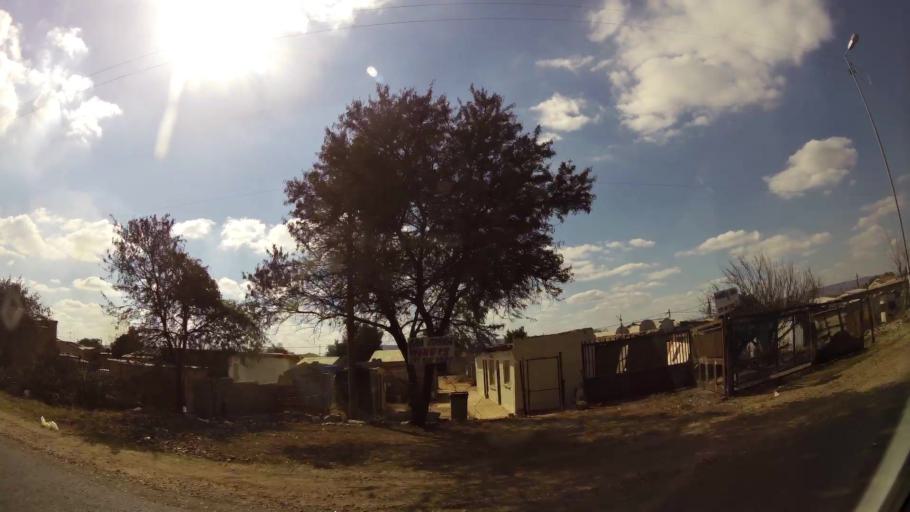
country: ZA
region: Gauteng
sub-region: City of Tshwane Metropolitan Municipality
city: Pretoria
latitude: -25.7460
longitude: 28.3536
